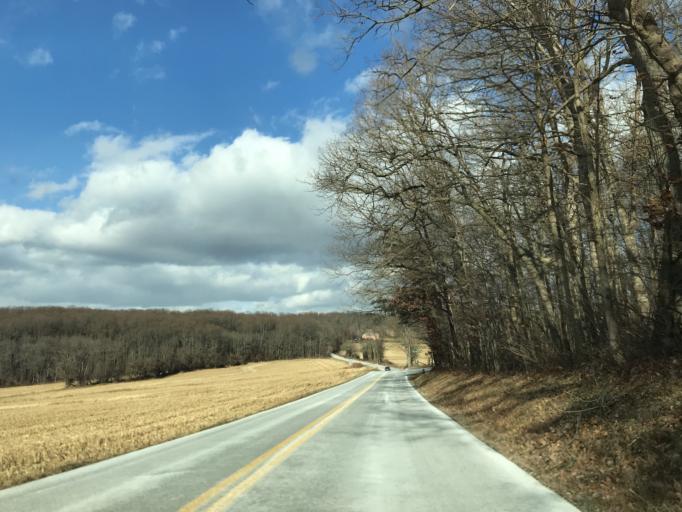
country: US
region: Maryland
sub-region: Baltimore County
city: Hunt Valley
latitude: 39.5739
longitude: -76.6572
